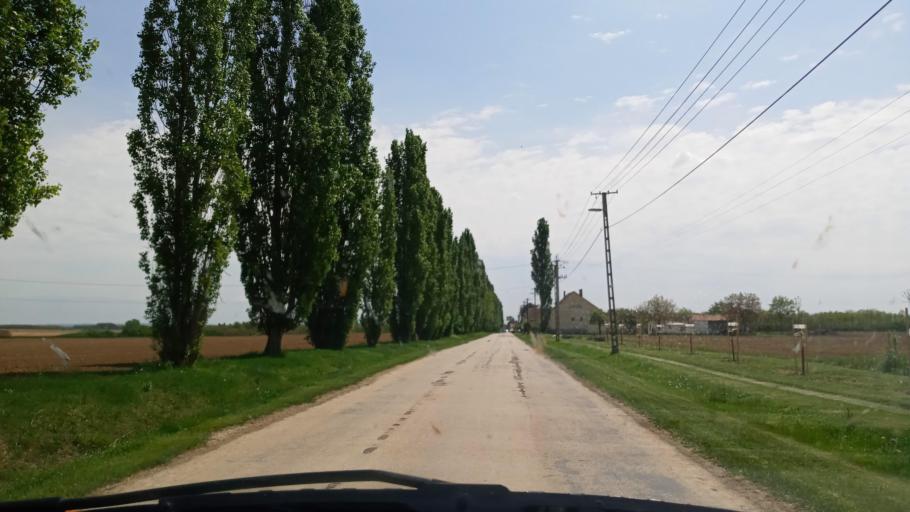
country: HU
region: Baranya
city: Villany
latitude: 45.8802
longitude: 18.5031
